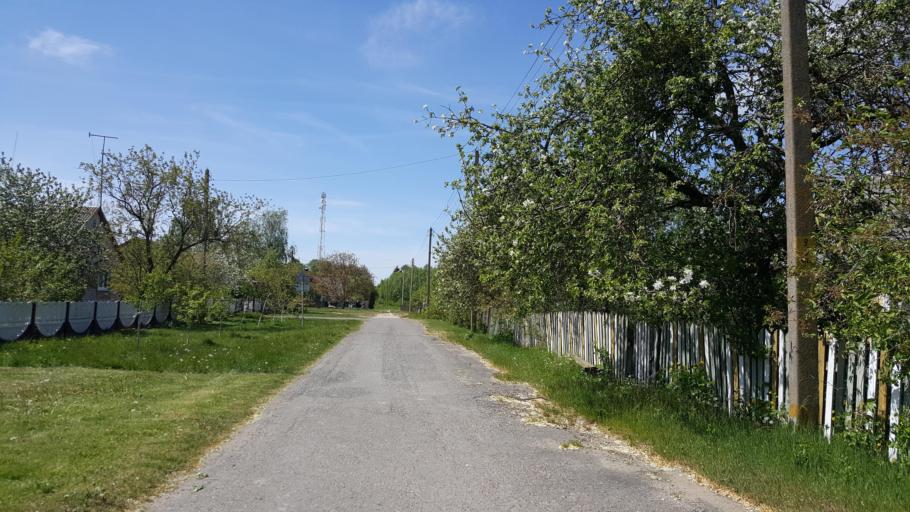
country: BY
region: Brest
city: Kobryn
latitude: 52.3397
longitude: 24.2478
